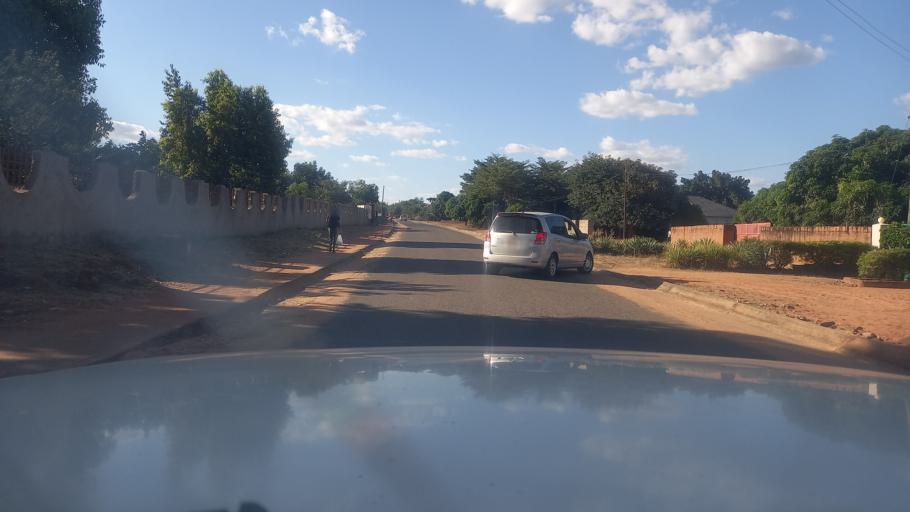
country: ZM
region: Southern
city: Livingstone
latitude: -17.8320
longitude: 25.8660
